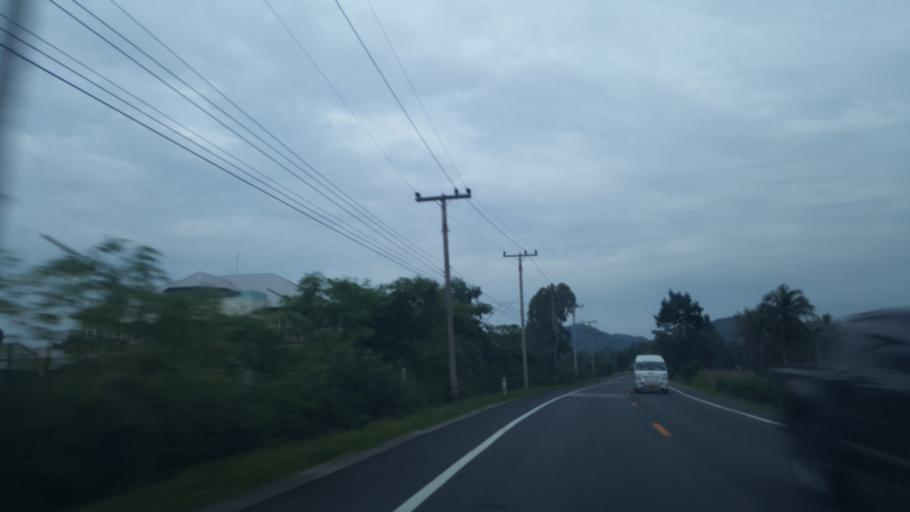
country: TH
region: Chon Buri
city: Ban Talat Bueng
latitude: 12.9852
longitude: 100.9975
